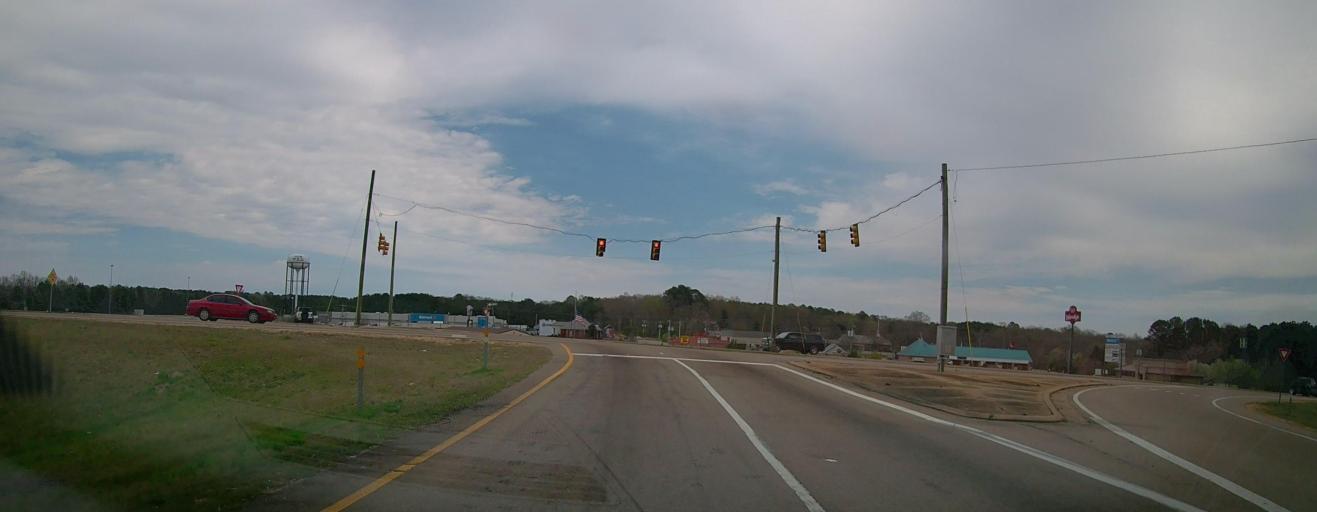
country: US
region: Mississippi
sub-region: Itawamba County
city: Fulton
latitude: 34.2400
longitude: -88.4019
